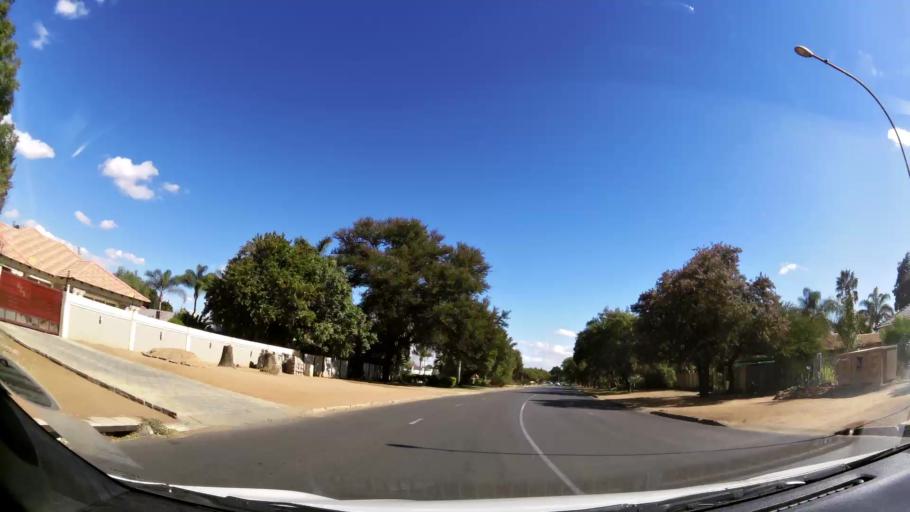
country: ZA
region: Limpopo
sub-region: Capricorn District Municipality
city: Polokwane
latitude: -23.9131
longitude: 29.4805
